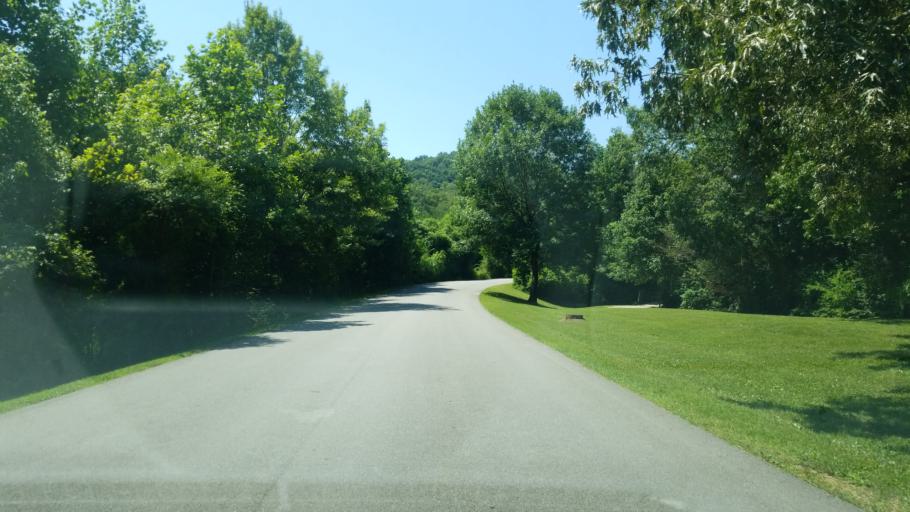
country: US
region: Tennessee
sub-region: Hamilton County
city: East Chattanooga
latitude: 35.1282
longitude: -85.2149
